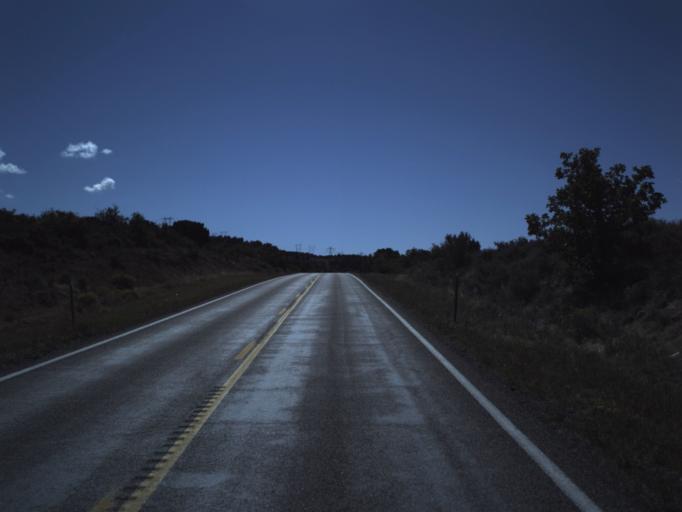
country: US
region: Utah
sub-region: Washington County
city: Enterprise
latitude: 37.4840
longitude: -113.6291
